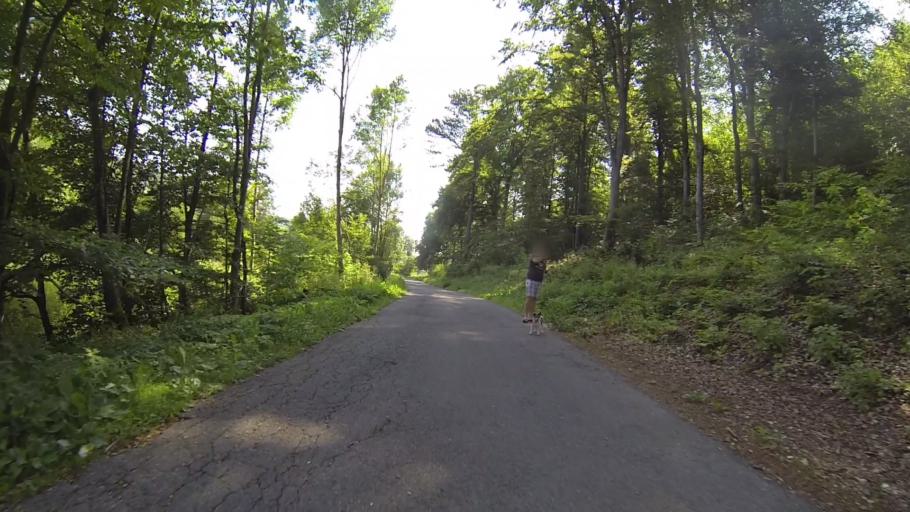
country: DE
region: Baden-Wuerttemberg
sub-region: Regierungsbezirk Stuttgart
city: Konigsbronn
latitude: 48.7339
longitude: 10.1239
